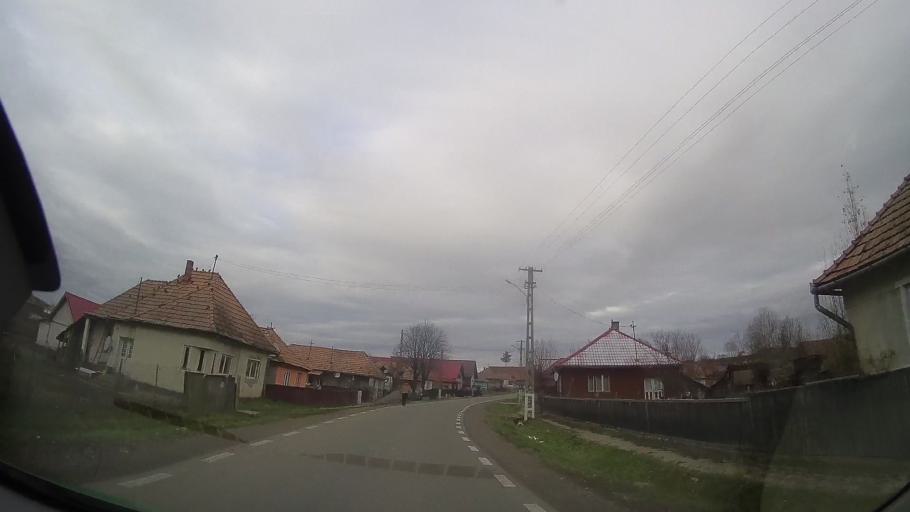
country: RO
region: Mures
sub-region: Comuna Faragau
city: Faragau
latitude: 46.7783
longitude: 24.5541
